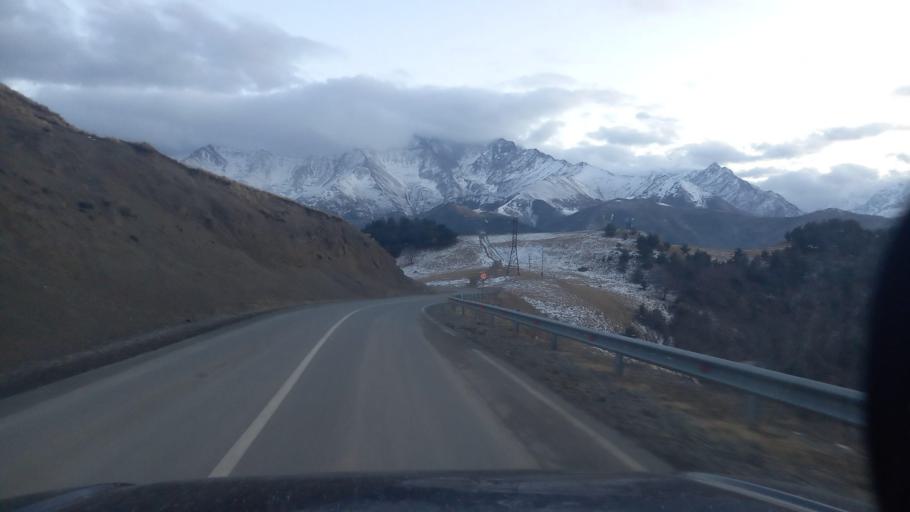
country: RU
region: Ingushetiya
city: Dzhayrakh
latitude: 42.8198
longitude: 44.8387
